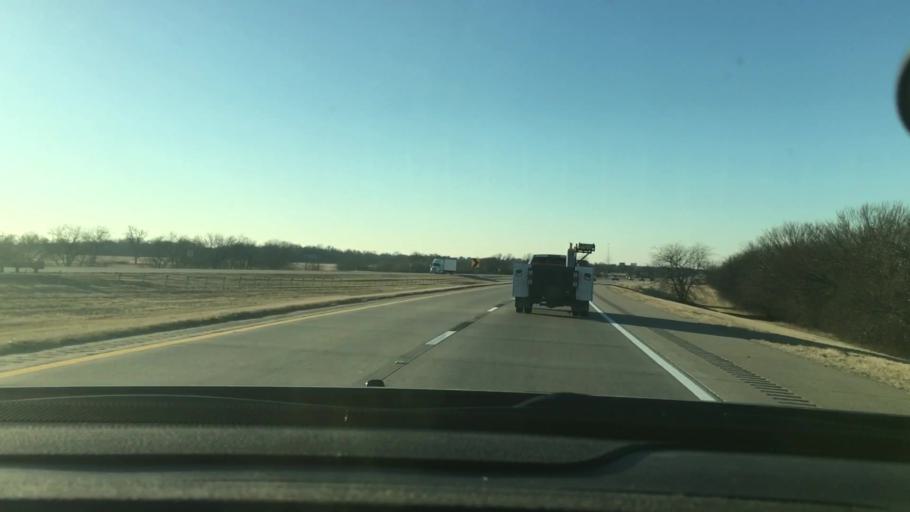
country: US
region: Oklahoma
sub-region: Murray County
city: Davis
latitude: 34.3463
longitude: -97.1480
